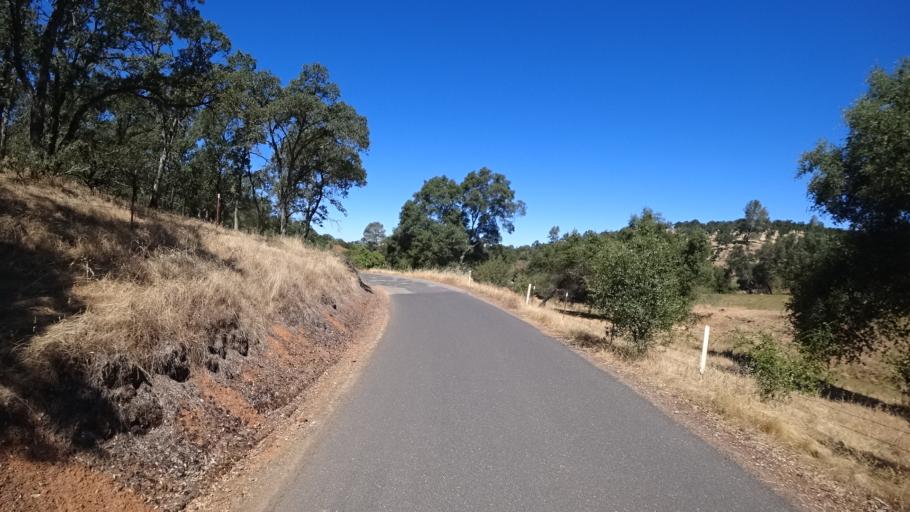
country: US
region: California
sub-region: Calaveras County
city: Rancho Calaveras
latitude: 38.0168
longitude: -120.7959
